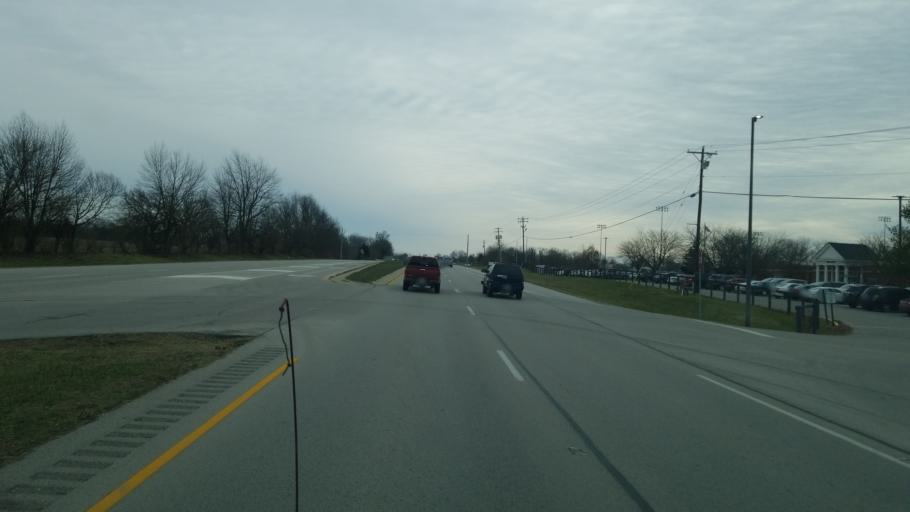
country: US
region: Kentucky
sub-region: Bourbon County
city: Paris
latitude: 38.2250
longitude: -84.2432
